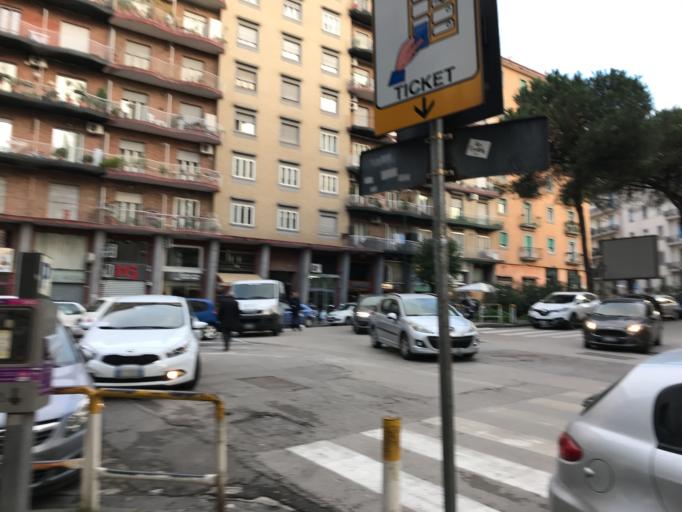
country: IT
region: Campania
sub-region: Provincia di Napoli
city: Napoli
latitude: 40.8502
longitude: 14.2275
